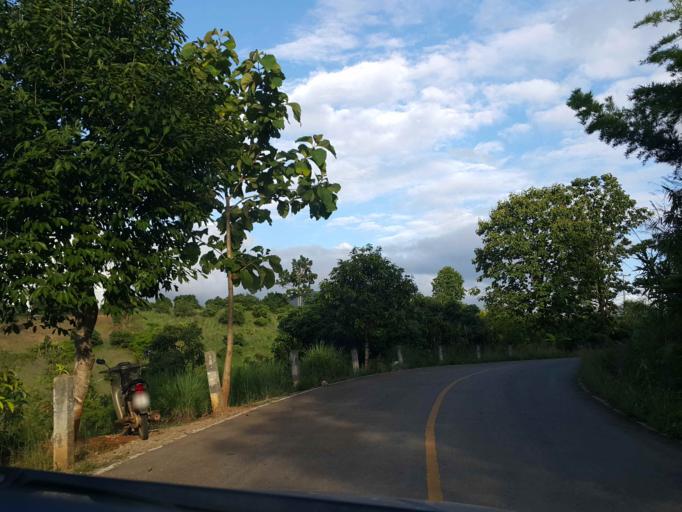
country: TH
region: Chiang Mai
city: Mae Chaem
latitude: 18.5125
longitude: 98.4073
